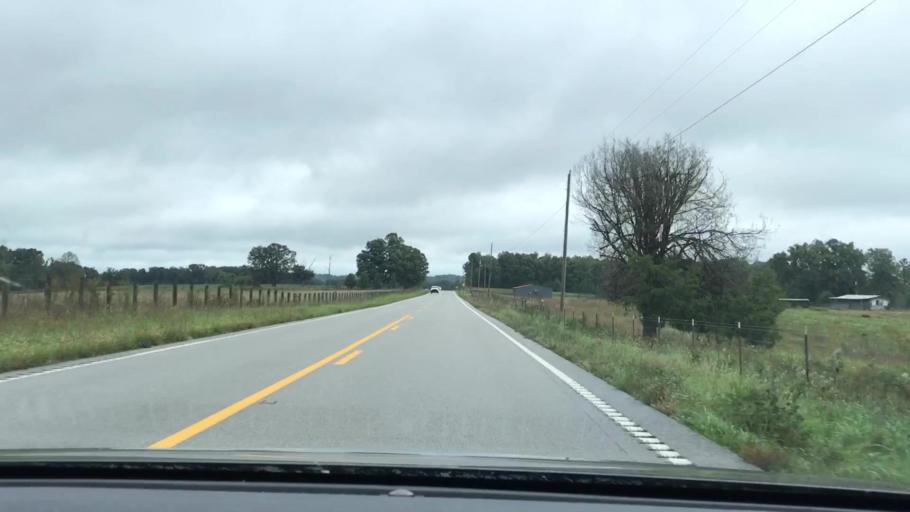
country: US
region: Tennessee
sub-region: Fentress County
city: Jamestown
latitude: 36.3643
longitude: -84.7513
